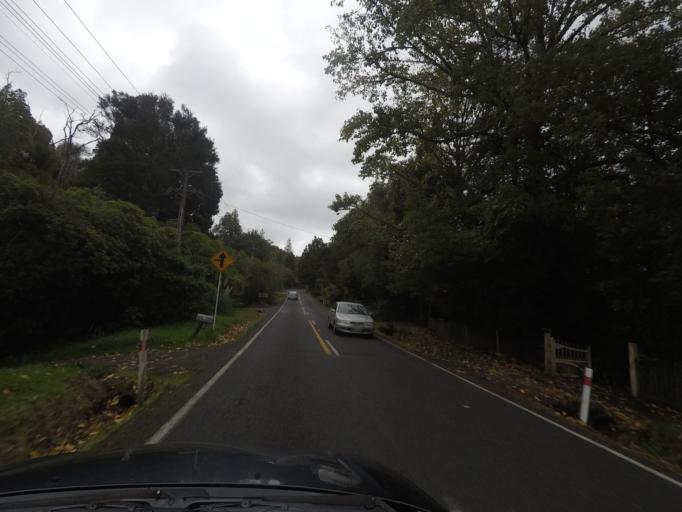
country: NZ
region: Auckland
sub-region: Auckland
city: Titirangi
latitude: -36.9313
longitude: 174.5914
